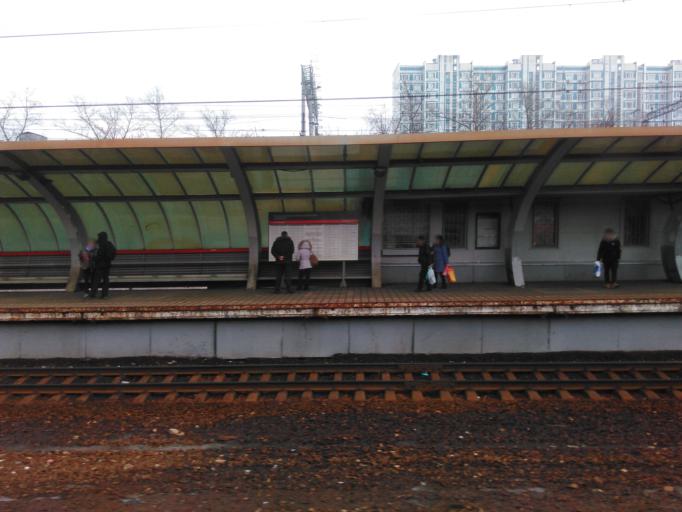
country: RU
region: Moscow
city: Yaroslavskiy
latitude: 55.8802
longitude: 37.7108
